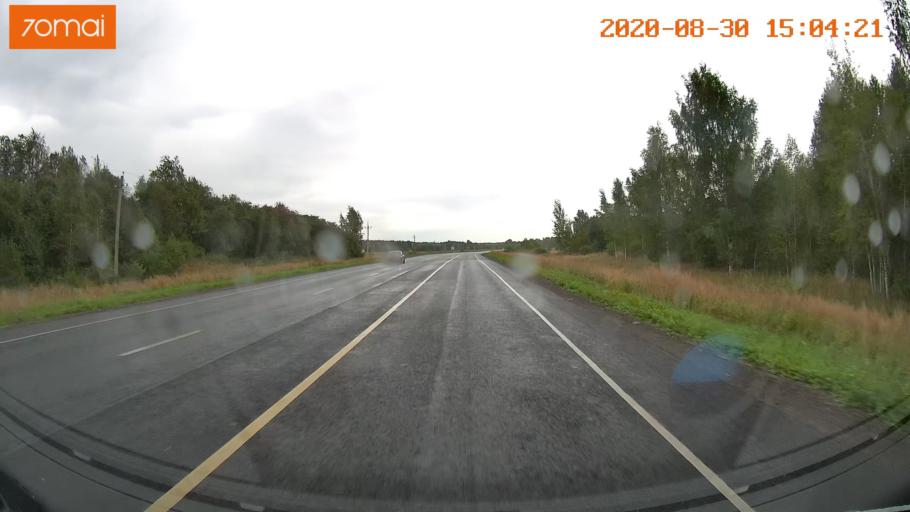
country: RU
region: Ivanovo
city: Staraya Vichuga
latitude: 57.2879
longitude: 41.9088
